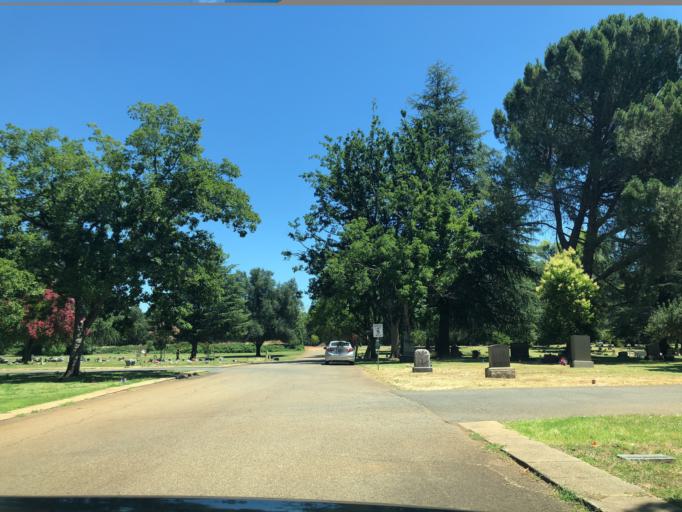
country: US
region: California
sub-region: Shasta County
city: Redding
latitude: 40.5891
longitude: -122.3865
